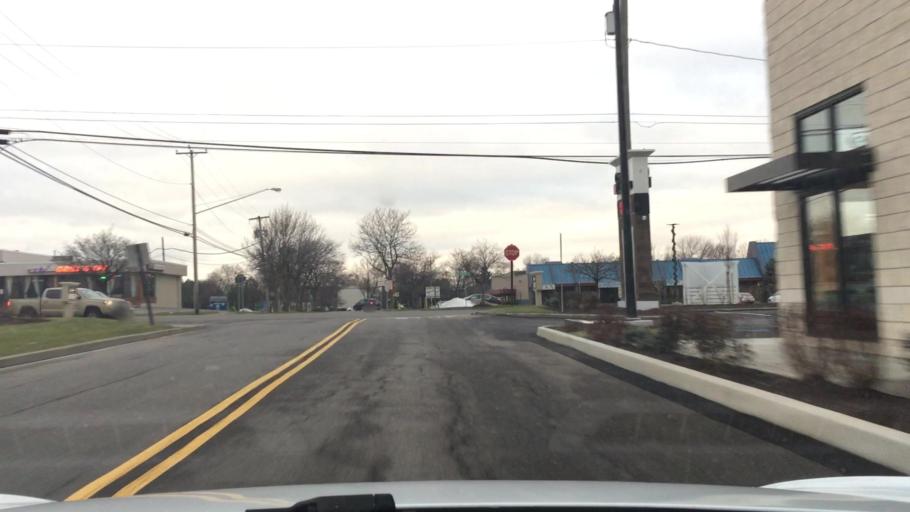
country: US
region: New York
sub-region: Erie County
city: Harris Hill
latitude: 42.9816
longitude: -78.6963
